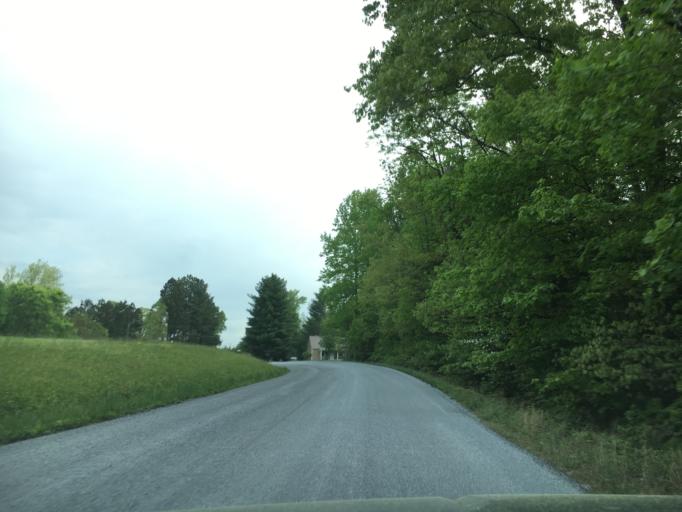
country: US
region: Virginia
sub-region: Campbell County
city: Brookneal
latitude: 36.9371
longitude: -78.9469
